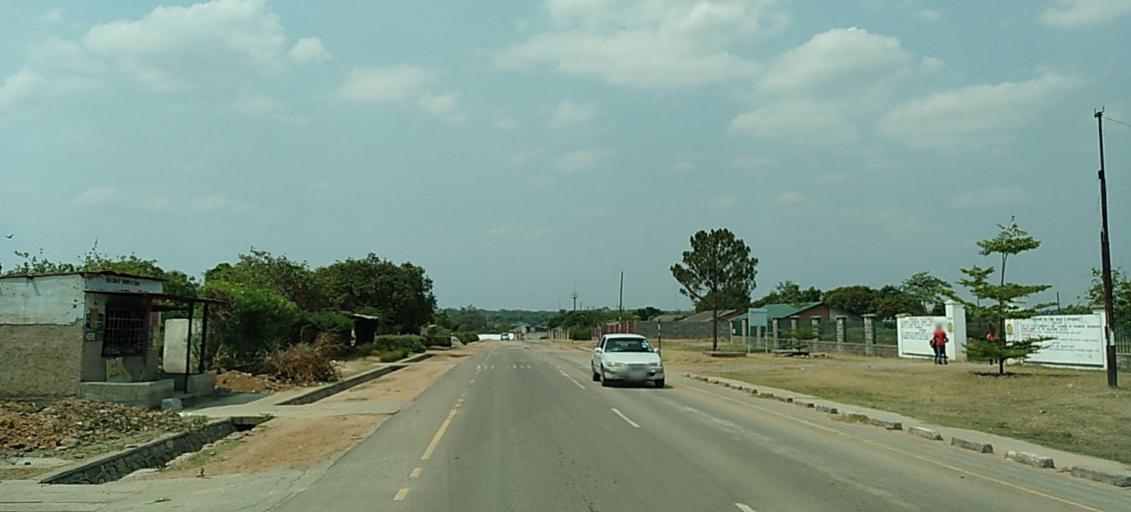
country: ZM
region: Copperbelt
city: Chambishi
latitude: -12.6332
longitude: 28.0585
